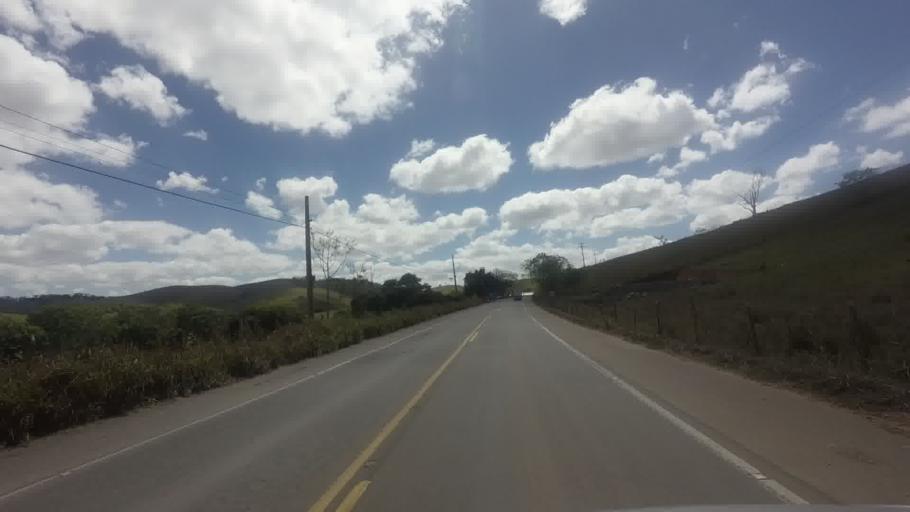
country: BR
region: Rio de Janeiro
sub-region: Santo Antonio De Padua
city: Santo Antonio de Padua
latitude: -21.6468
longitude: -42.2840
